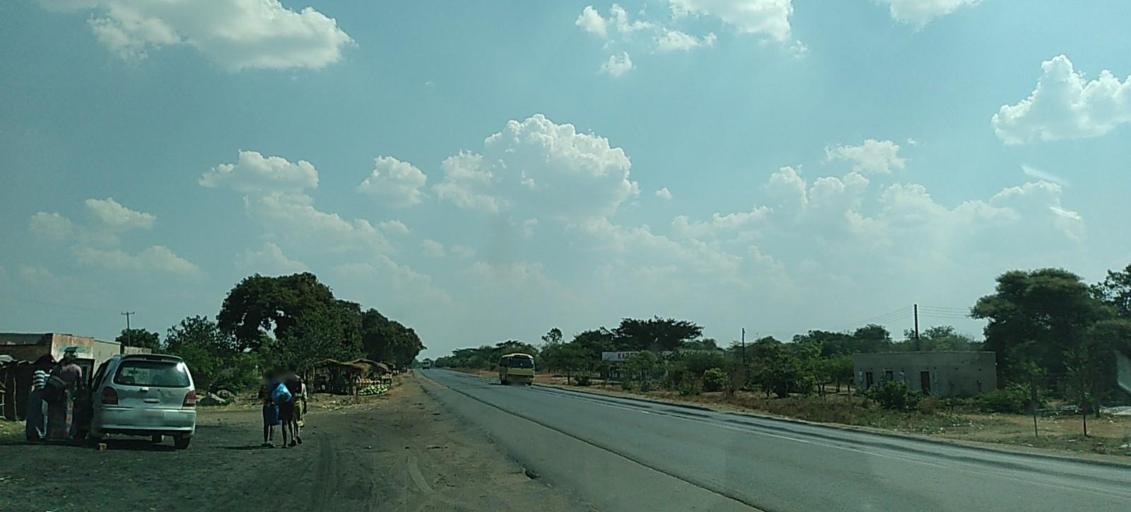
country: ZM
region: Central
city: Chibombo
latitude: -14.7249
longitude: 28.0803
